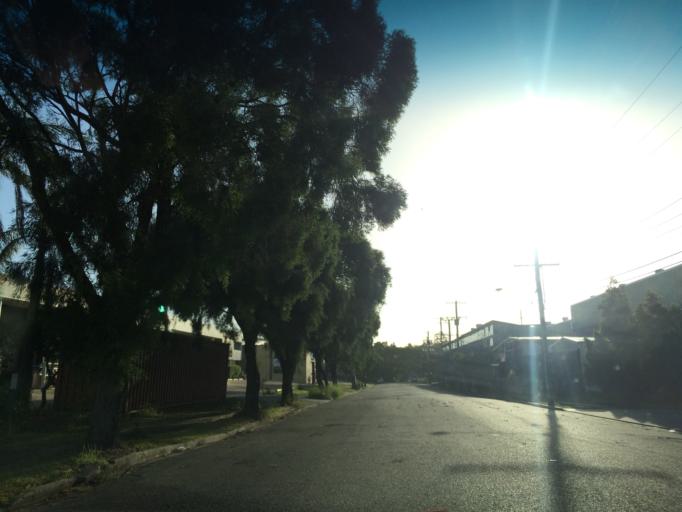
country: AU
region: Queensland
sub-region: Brisbane
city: Woolloongabba
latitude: -27.4886
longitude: 153.0545
